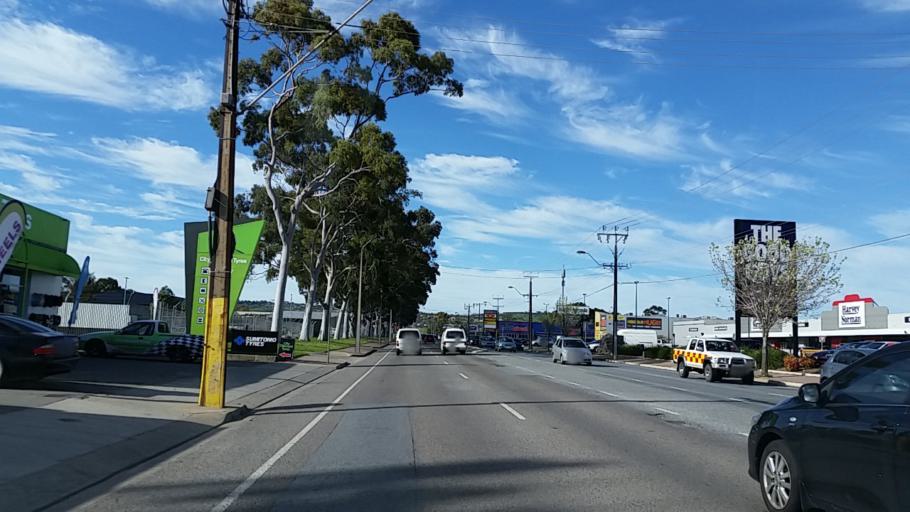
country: AU
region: South Australia
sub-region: Marion
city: Marion
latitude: -35.0106
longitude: 138.5584
